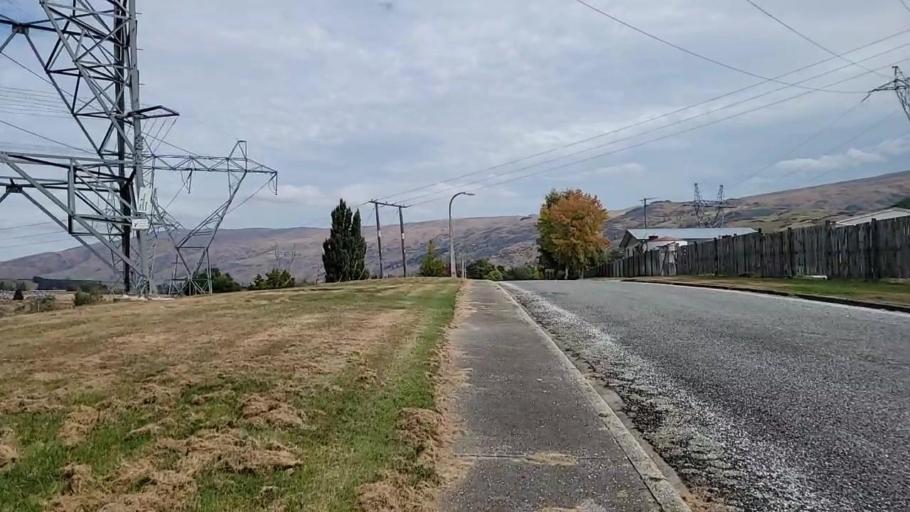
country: NZ
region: Otago
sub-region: Queenstown-Lakes District
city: Kingston
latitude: -45.4767
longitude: 169.3183
